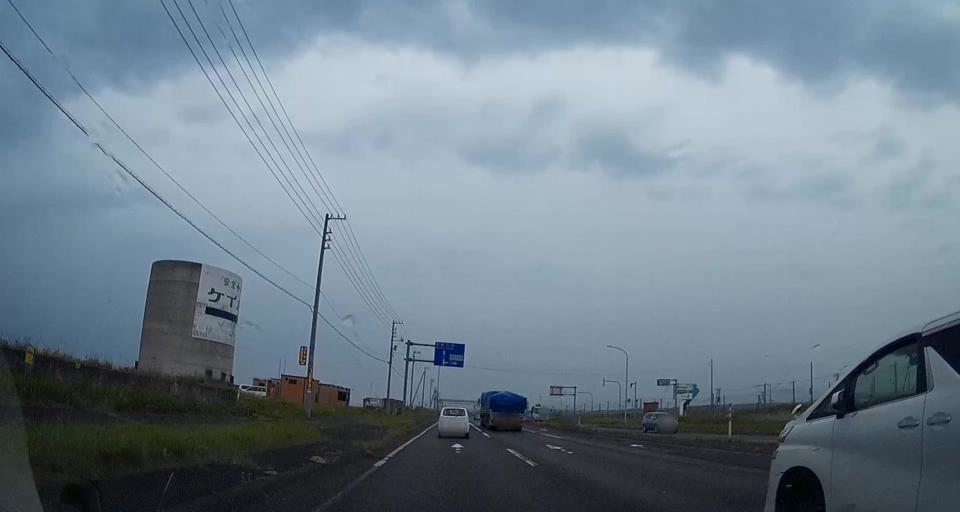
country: JP
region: Hokkaido
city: Shiraoi
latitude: 42.5936
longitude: 141.4635
